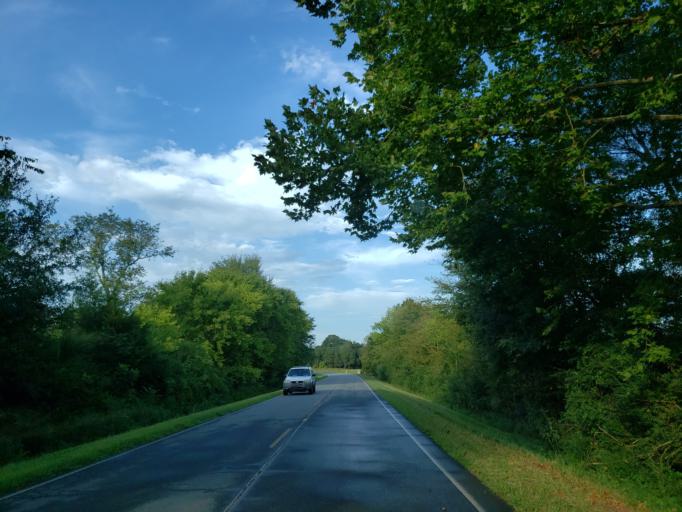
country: US
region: Georgia
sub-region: Bartow County
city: Euharlee
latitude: 34.2294
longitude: -84.9586
